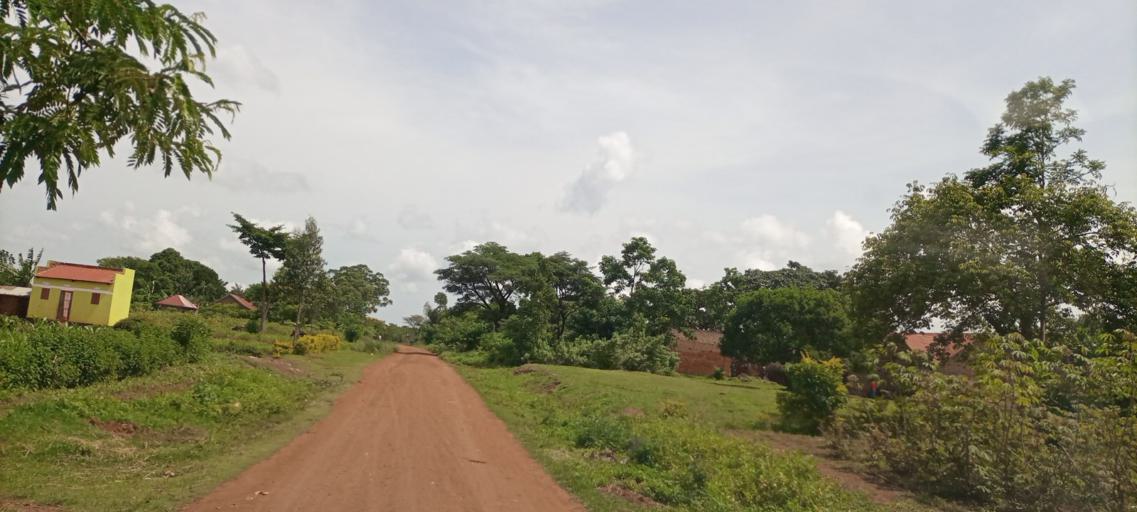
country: UG
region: Eastern Region
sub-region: Budaka District
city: Budaka
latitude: 1.1745
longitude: 33.9266
